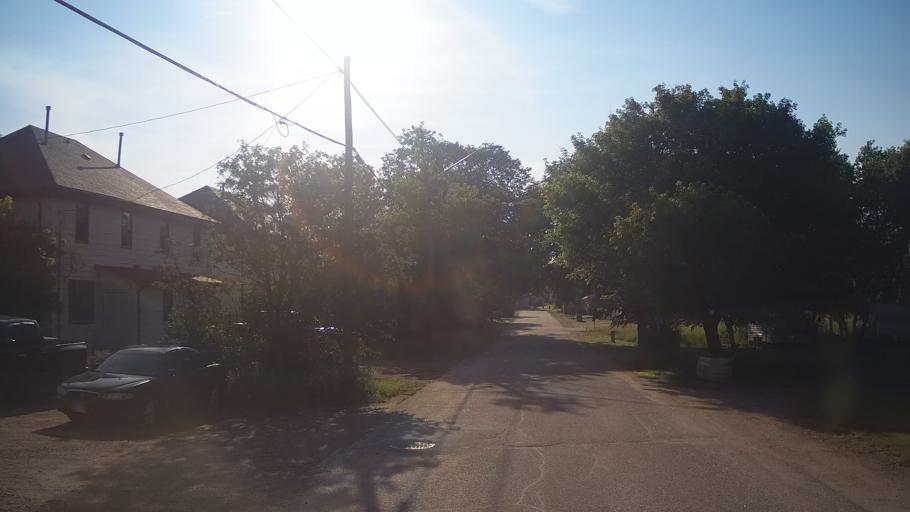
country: CA
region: Ontario
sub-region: Rainy River District
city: Atikokan
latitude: 49.4181
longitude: -91.6600
